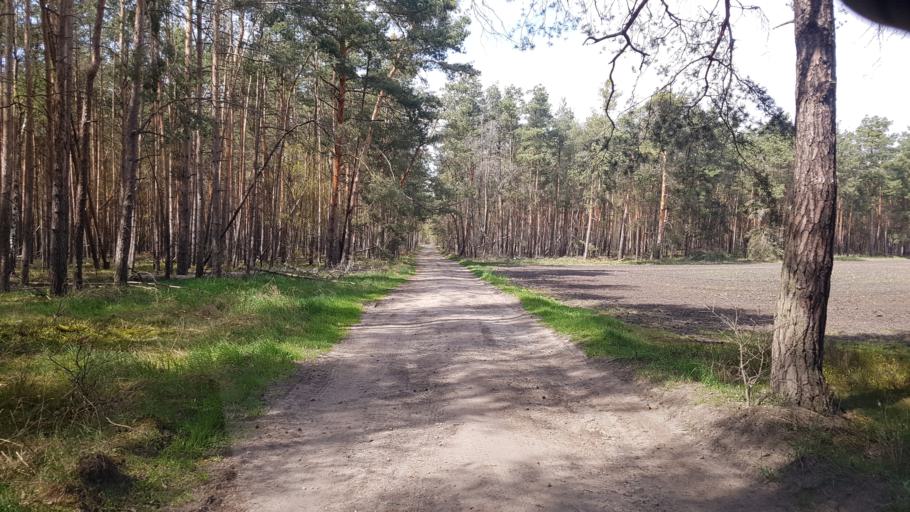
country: DE
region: Brandenburg
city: Plessa
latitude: 51.5423
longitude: 13.6618
